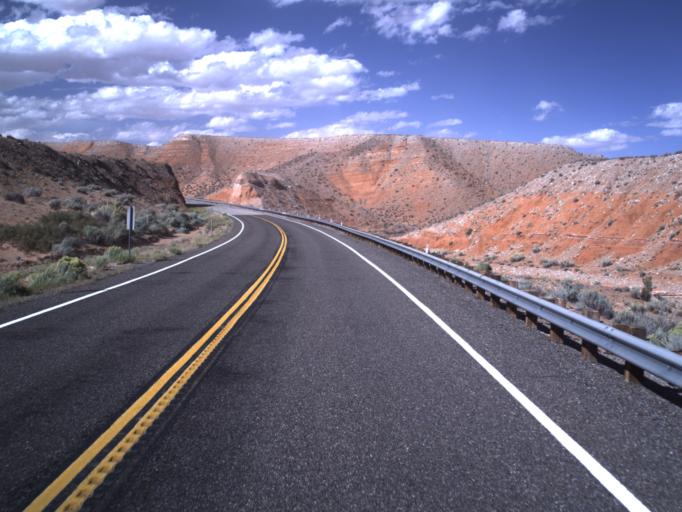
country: US
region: Utah
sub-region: Wayne County
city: Loa
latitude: 38.1386
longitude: -110.6095
